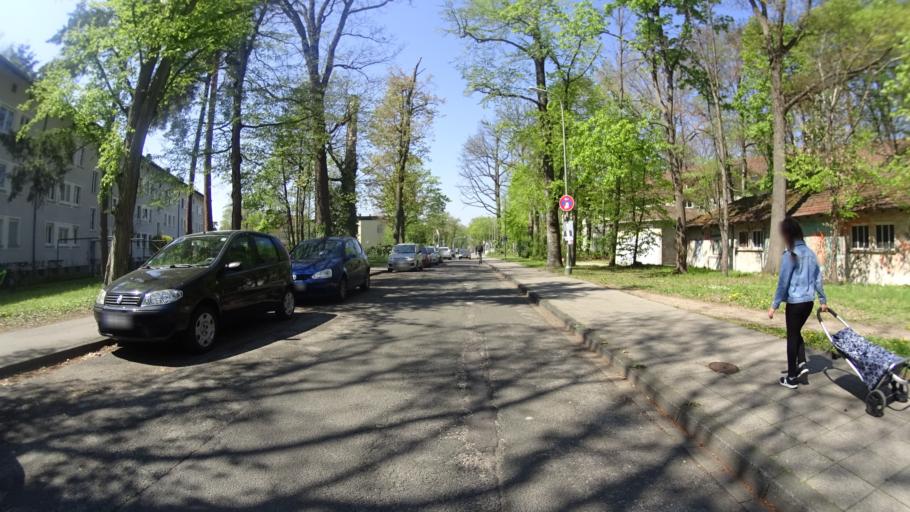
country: DE
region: Baden-Wuerttemberg
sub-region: Karlsruhe Region
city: Karlsruhe
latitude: 49.0171
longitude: 8.3870
